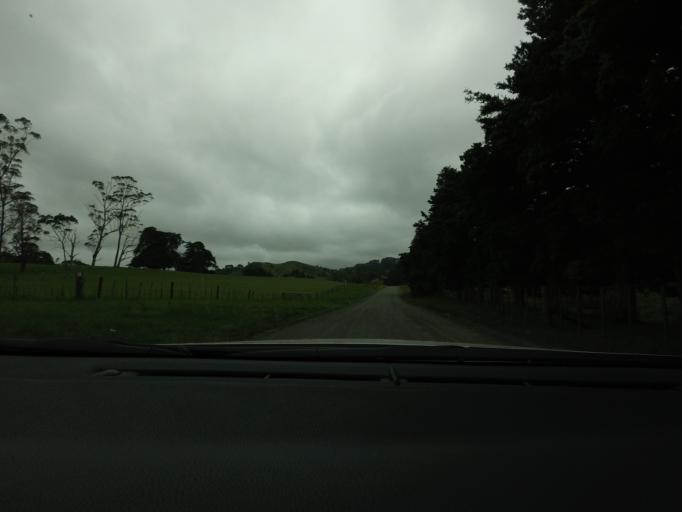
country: NZ
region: Auckland
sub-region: Auckland
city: Warkworth
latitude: -36.4782
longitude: 174.5839
